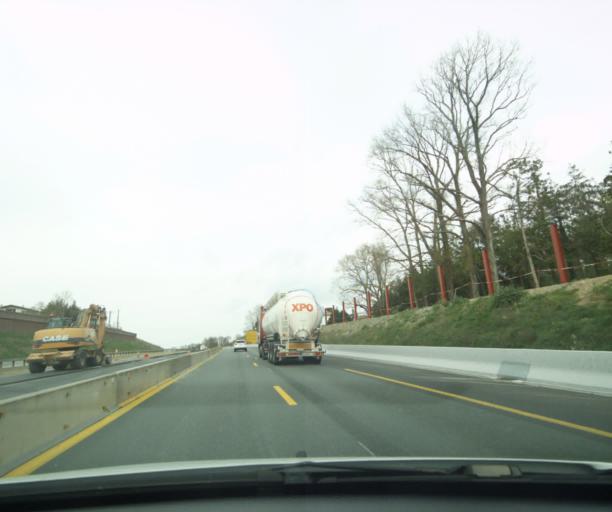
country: FR
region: Aquitaine
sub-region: Departement des Pyrenees-Atlantiques
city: Saint-Jean-de-Luz
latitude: 43.3906
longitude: -1.6395
